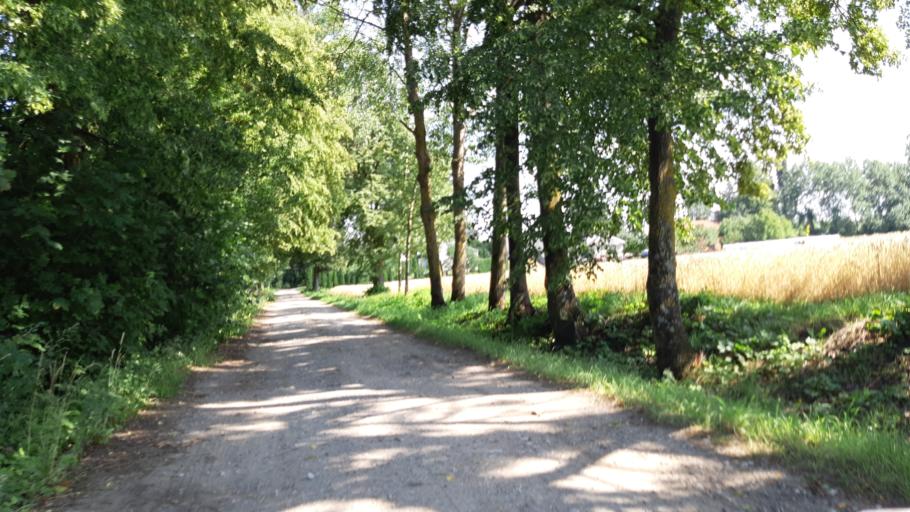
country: LT
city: Virbalis
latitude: 54.6330
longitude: 22.8267
